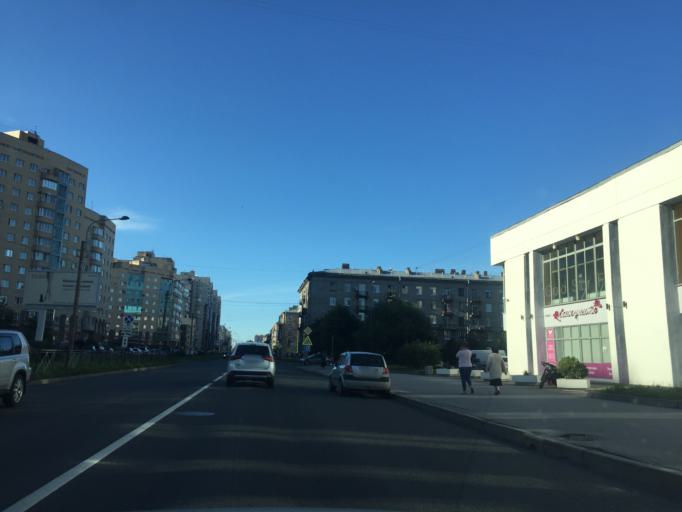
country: RU
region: St.-Petersburg
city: Kupchino
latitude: 59.8689
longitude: 30.3139
